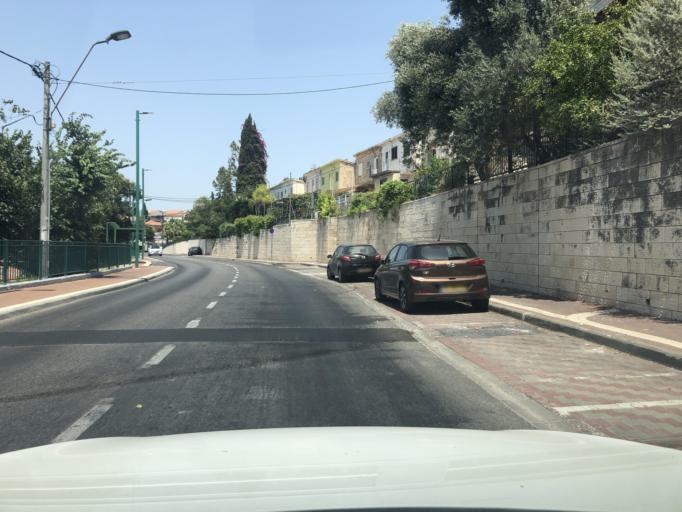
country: IL
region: Haifa
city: Daliyat el Karmil
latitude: 32.6571
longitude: 35.1074
